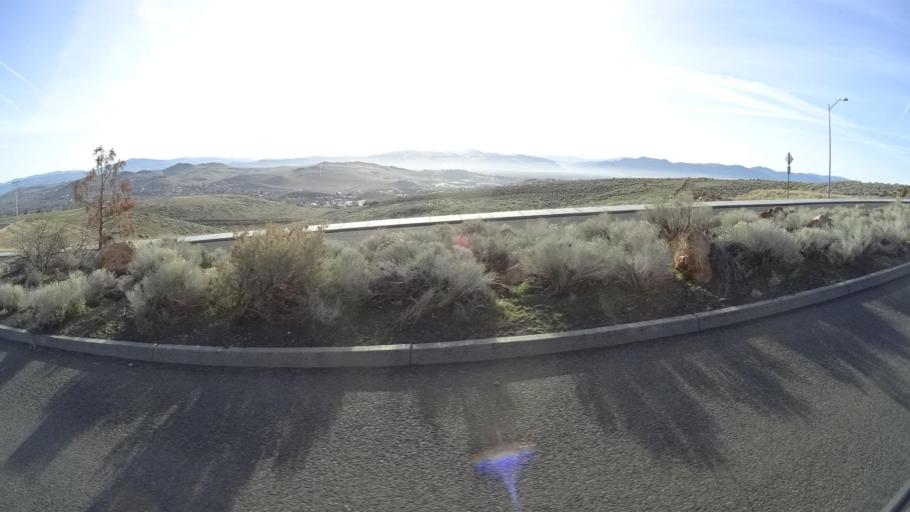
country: US
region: Nevada
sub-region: Washoe County
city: Sun Valley
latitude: 39.5713
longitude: -119.7937
